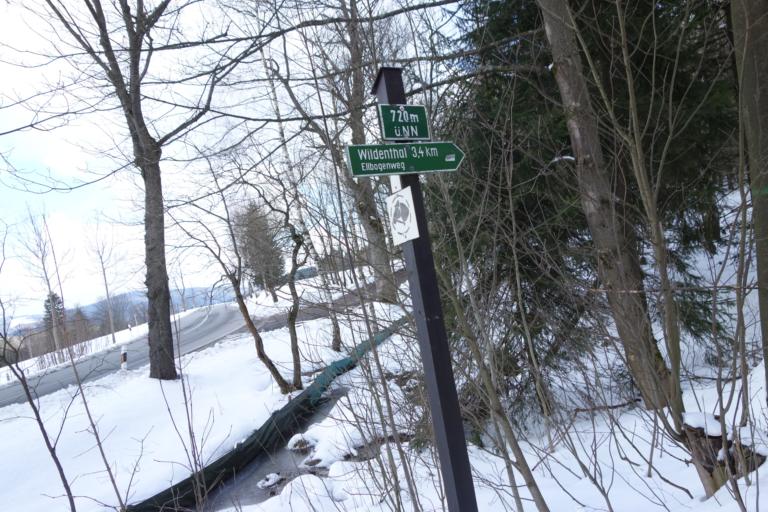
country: DE
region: Saxony
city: Eibenstock
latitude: 50.4762
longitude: 12.6171
